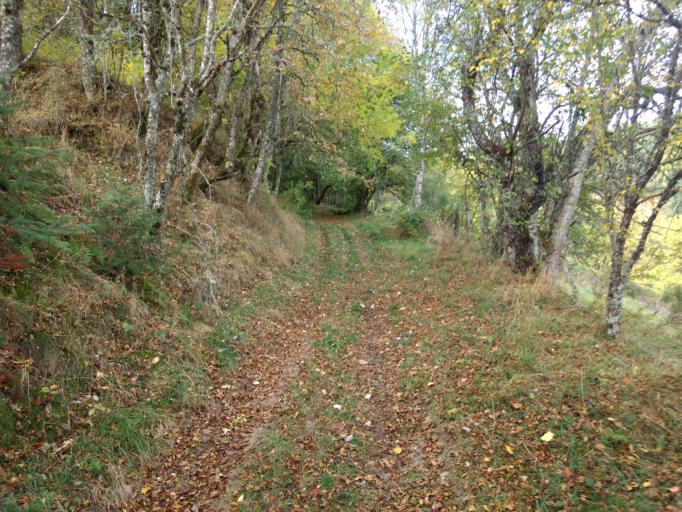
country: FR
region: Auvergne
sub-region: Departement du Cantal
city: Chaudes-Aigues
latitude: 44.8566
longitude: 2.9992
